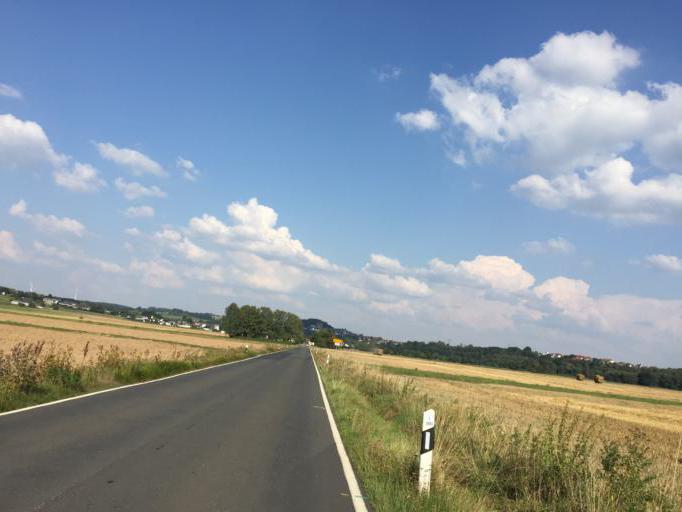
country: DE
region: Hesse
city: Lollar
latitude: 50.6570
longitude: 8.6946
